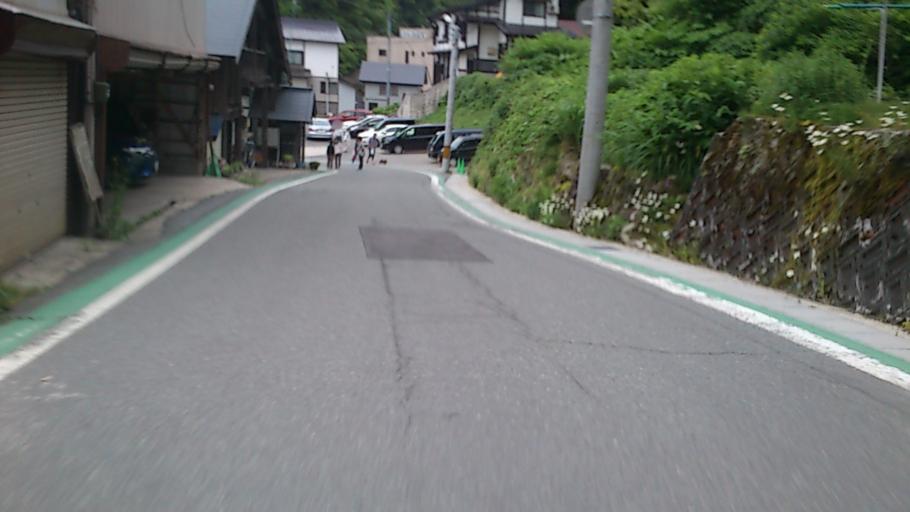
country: JP
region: Yamagata
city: Obanazawa
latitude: 38.5712
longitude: 140.5290
